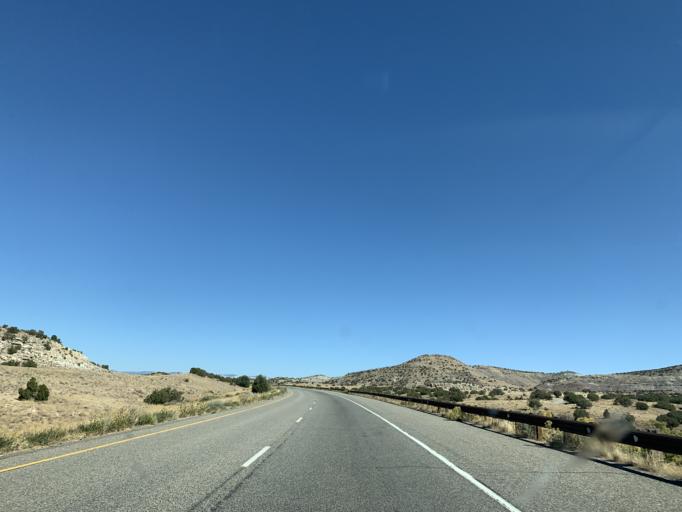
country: US
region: Colorado
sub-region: Mesa County
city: Loma
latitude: 39.2099
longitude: -108.9711
